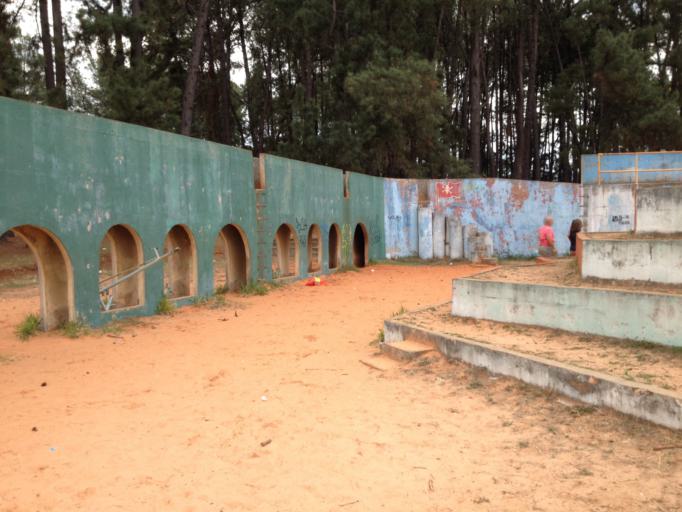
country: BR
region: Federal District
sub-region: Brasilia
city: Brasilia
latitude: -15.8051
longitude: -47.9181
